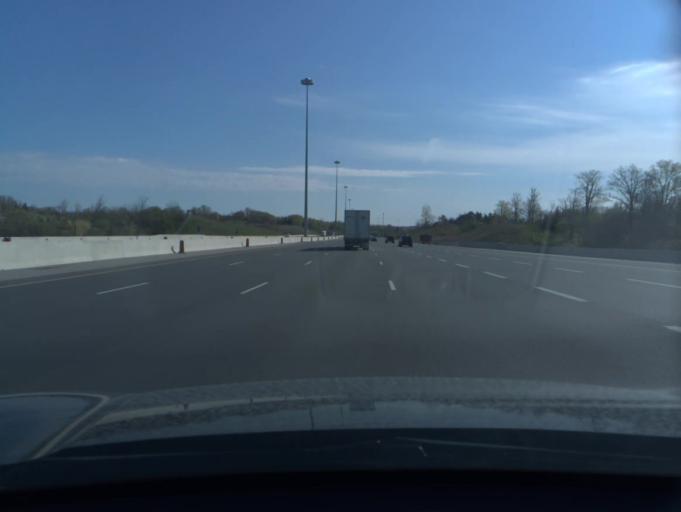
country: CA
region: Ontario
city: North Perth
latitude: 43.8139
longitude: -80.9999
